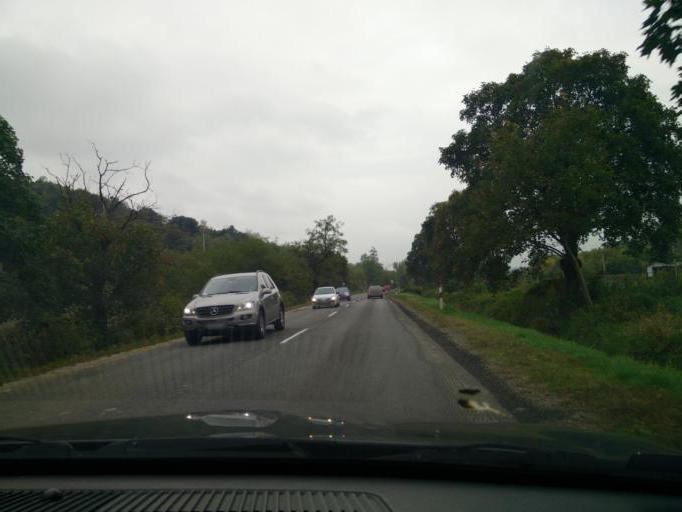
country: HU
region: Komarom-Esztergom
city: Piliscsev
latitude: 47.6681
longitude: 18.7805
